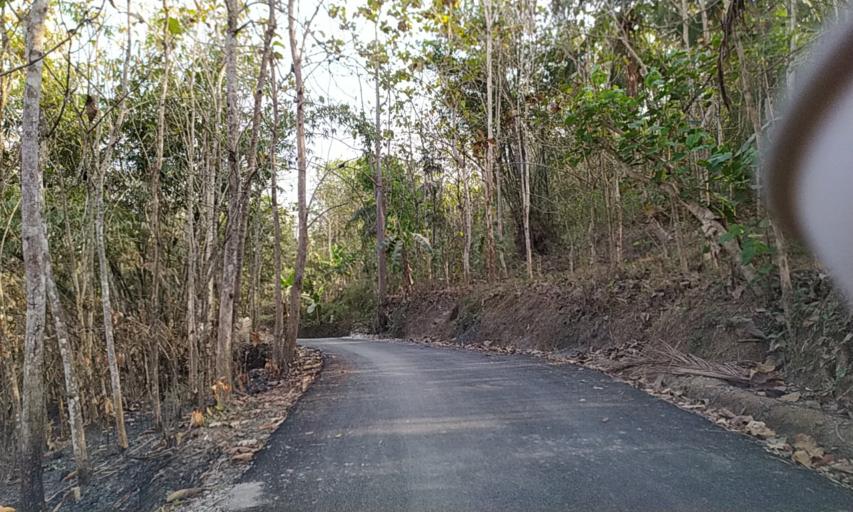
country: ID
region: Central Java
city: Bantarmangu
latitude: -7.3522
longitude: 108.8680
